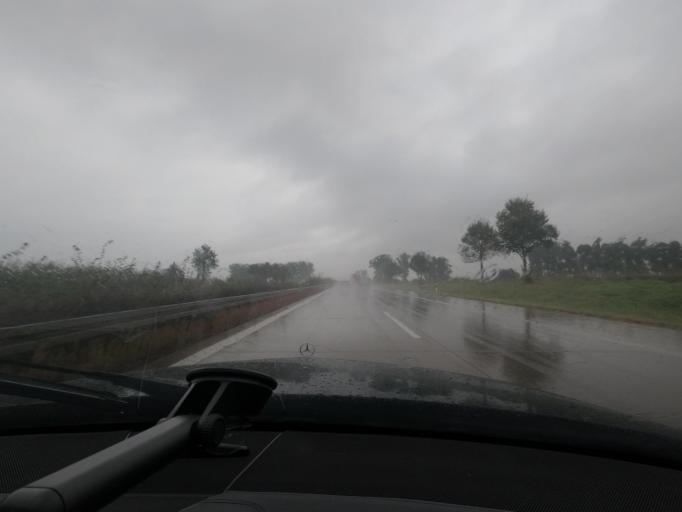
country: DE
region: Saxony-Anhalt
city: Bornstedt
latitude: 51.4386
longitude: 11.4450
